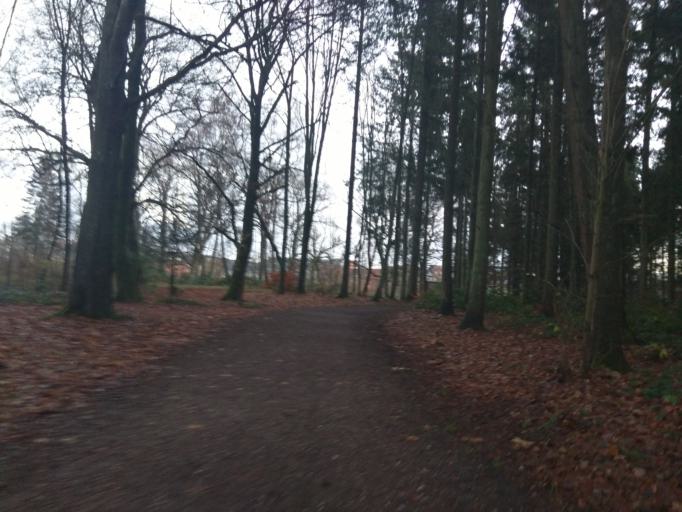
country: DK
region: Central Jutland
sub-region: Silkeborg Kommune
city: Silkeborg
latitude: 56.1718
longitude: 9.5409
